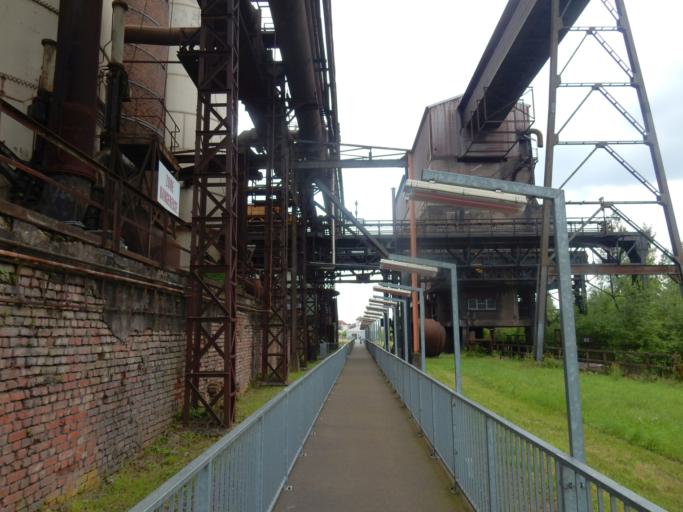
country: FR
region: Lorraine
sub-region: Departement de la Moselle
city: Uckange
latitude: 49.3066
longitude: 6.1566
